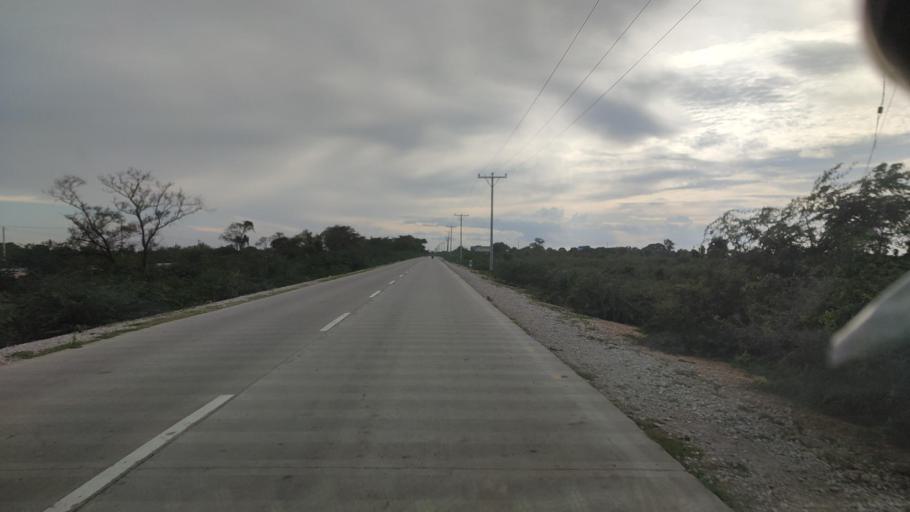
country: MM
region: Mandalay
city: Kyaukse
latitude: 21.3457
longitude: 96.0935
